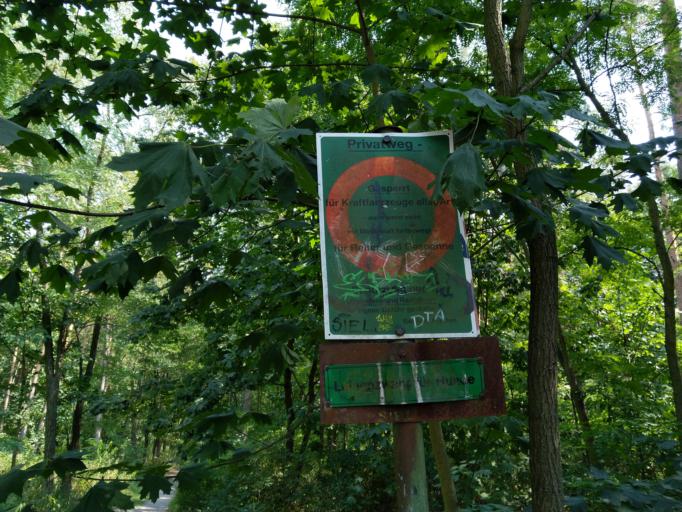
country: DE
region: Berlin
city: Berlin Koepenick
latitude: 52.4613
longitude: 13.5962
